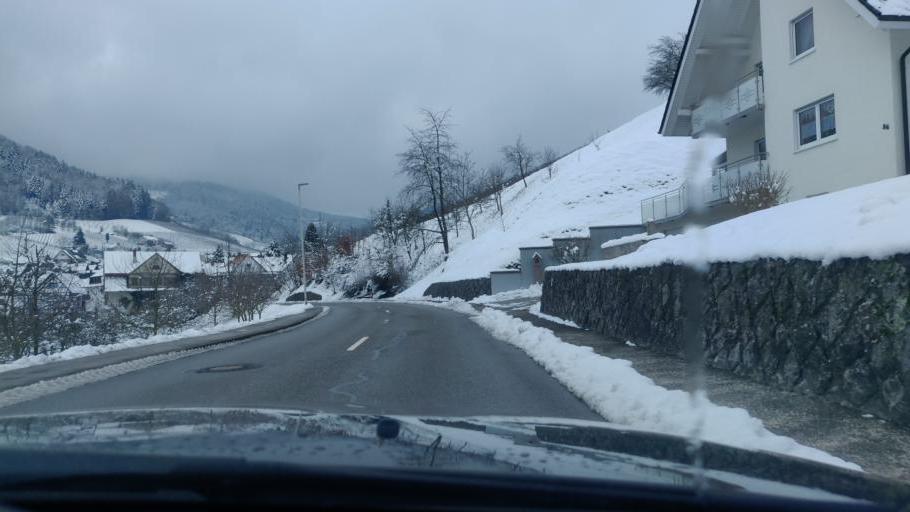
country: DE
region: Baden-Wuerttemberg
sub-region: Freiburg Region
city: Kappelrodeck
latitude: 48.5839
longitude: 8.1032
